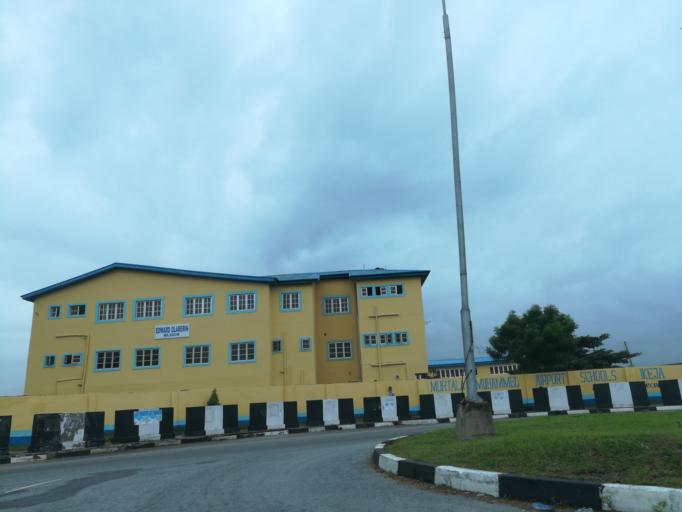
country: NG
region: Lagos
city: Ikeja
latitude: 6.5833
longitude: 3.3339
